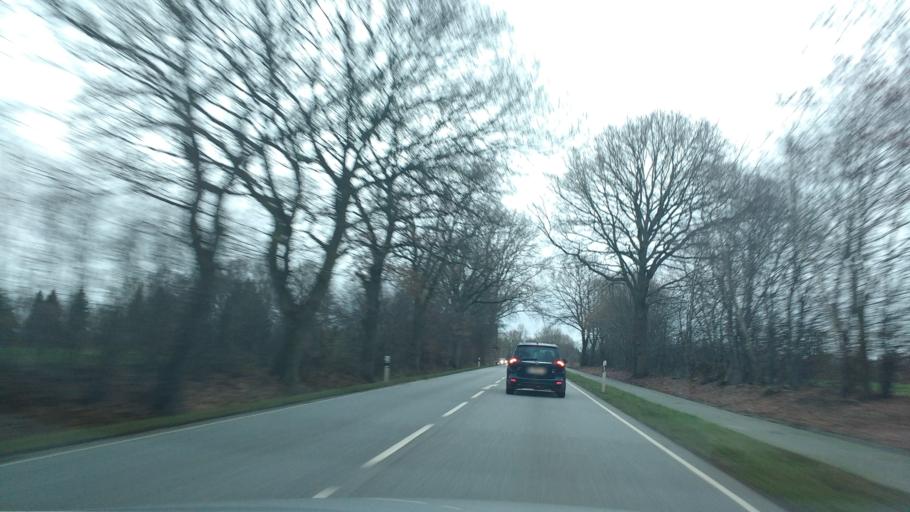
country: DE
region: Schleswig-Holstein
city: Oelixdorf
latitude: 53.9550
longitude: 9.5572
